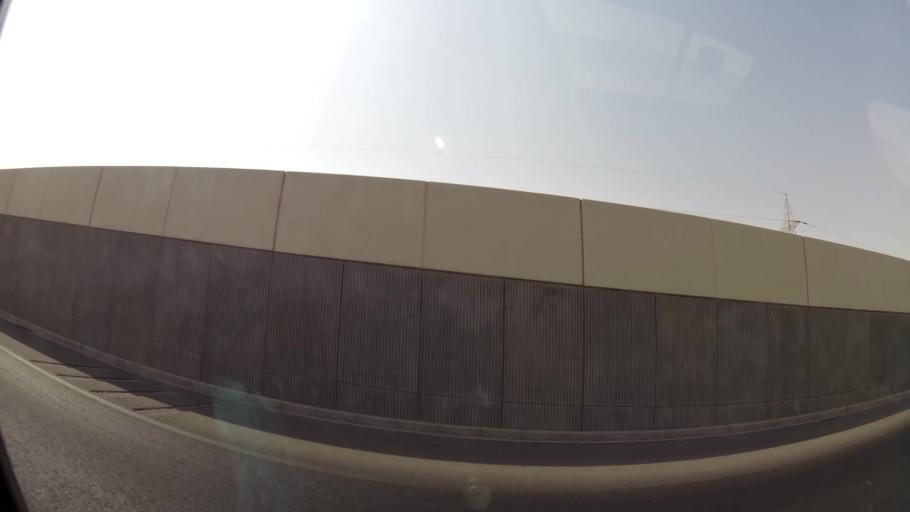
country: KW
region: Muhafazat al Jahra'
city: Al Jahra'
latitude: 29.3136
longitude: 47.6519
